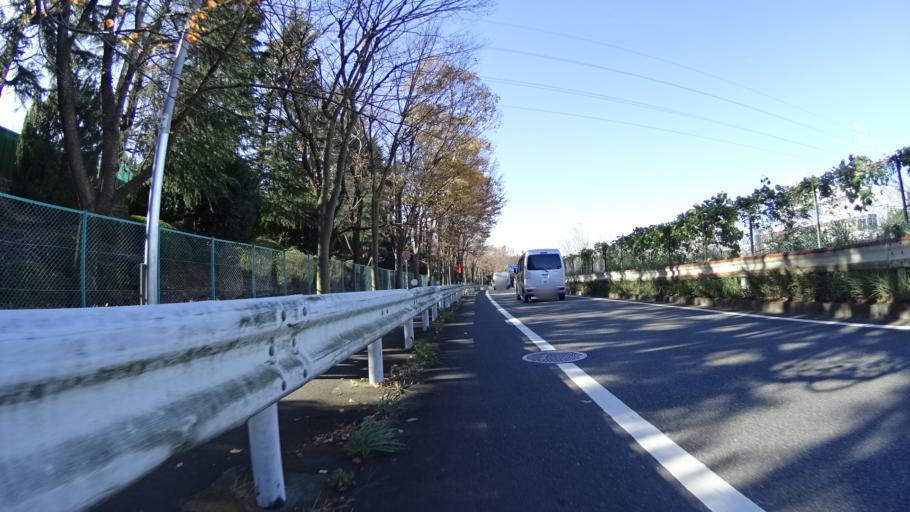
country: JP
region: Tokyo
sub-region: Machida-shi
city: Machida
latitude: 35.6118
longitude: 139.4470
